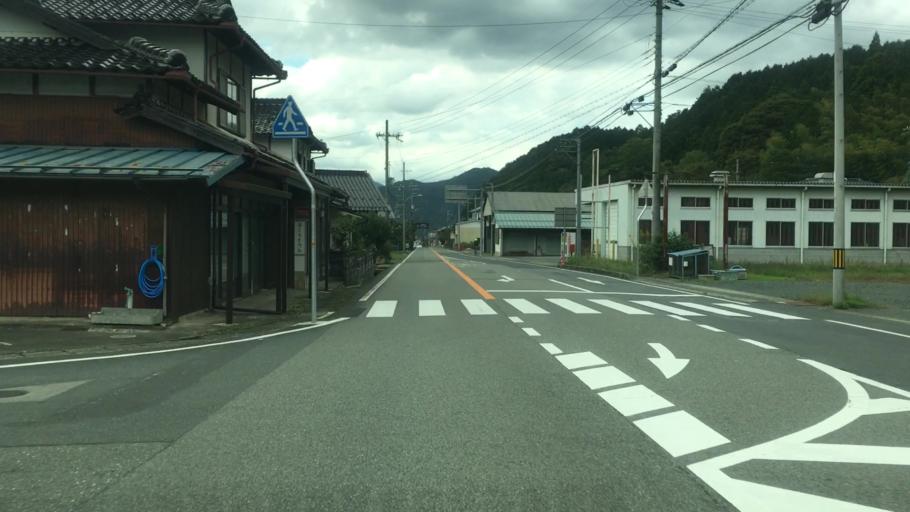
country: JP
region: Kyoto
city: Fukuchiyama
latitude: 35.3071
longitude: 134.9054
